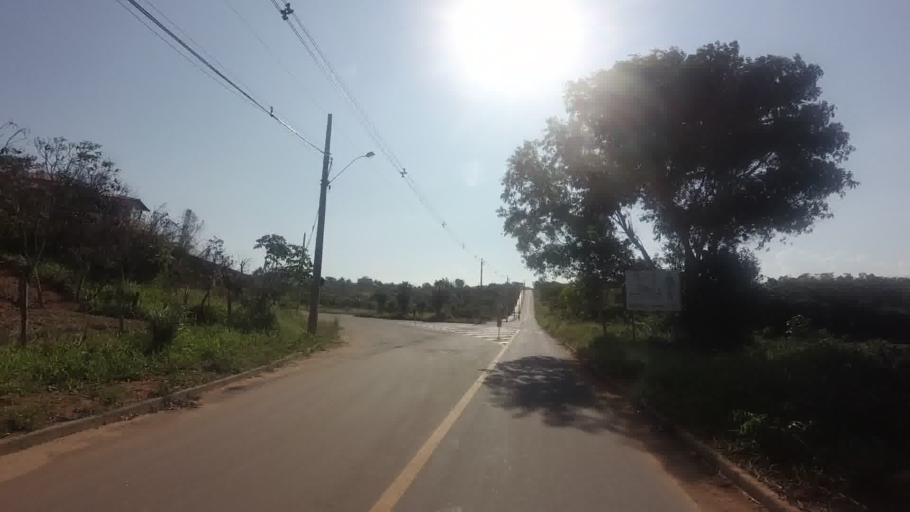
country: BR
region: Espirito Santo
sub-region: Guarapari
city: Guarapari
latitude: -20.7198
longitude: -40.5276
